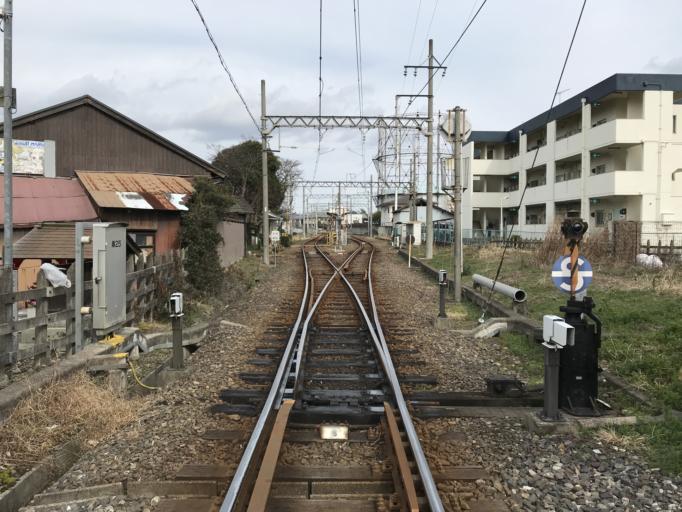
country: JP
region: Mie
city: Ueno-ebisumachi
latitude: 34.7609
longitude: 136.1353
